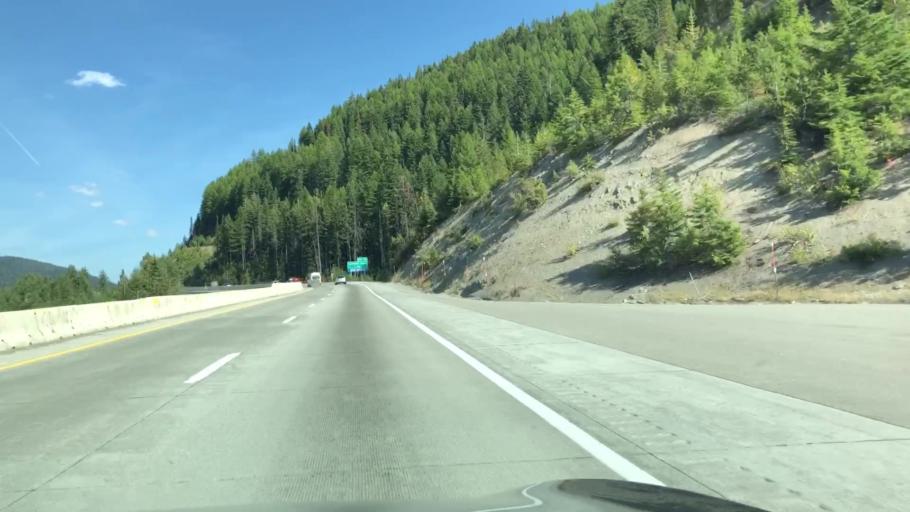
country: US
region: Idaho
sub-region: Shoshone County
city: Wallace
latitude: 47.4624
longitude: -115.7074
